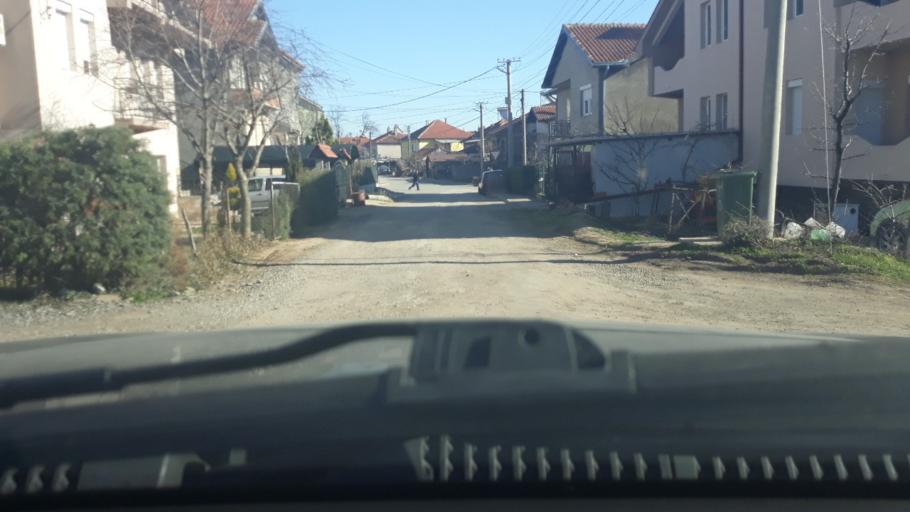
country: MK
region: Sveti Nikole
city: Sveti Nikole
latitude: 41.8709
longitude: 21.9319
